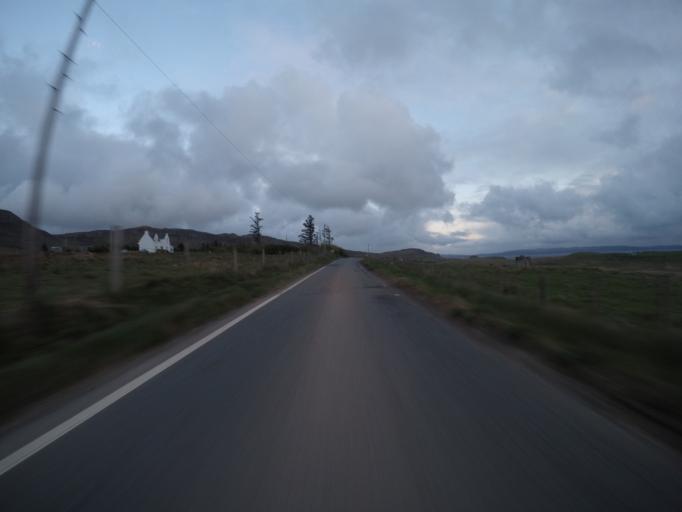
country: GB
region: Scotland
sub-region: Highland
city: Portree
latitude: 57.6273
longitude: -6.3777
